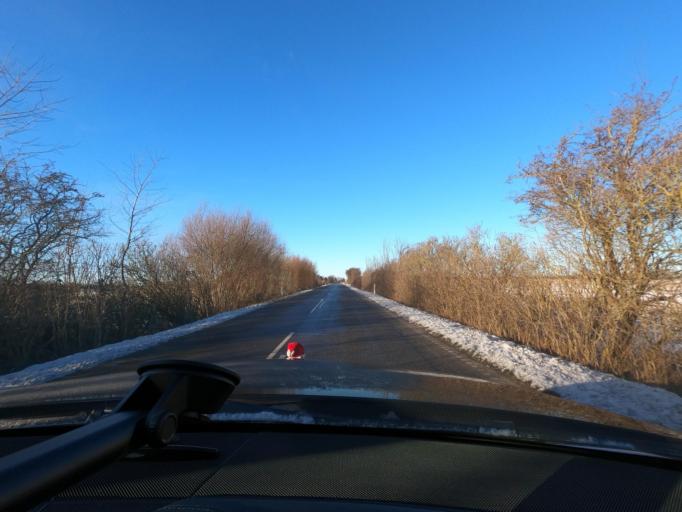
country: DK
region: South Denmark
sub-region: Sonderborg Kommune
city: Horuphav
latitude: 54.8595
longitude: 9.9731
